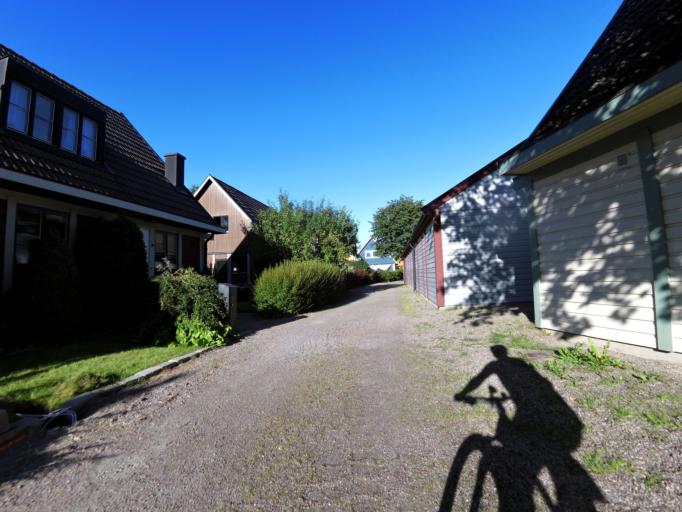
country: SE
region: Gaevleborg
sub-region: Gavle Kommun
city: Gavle
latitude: 60.6507
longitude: 17.1457
